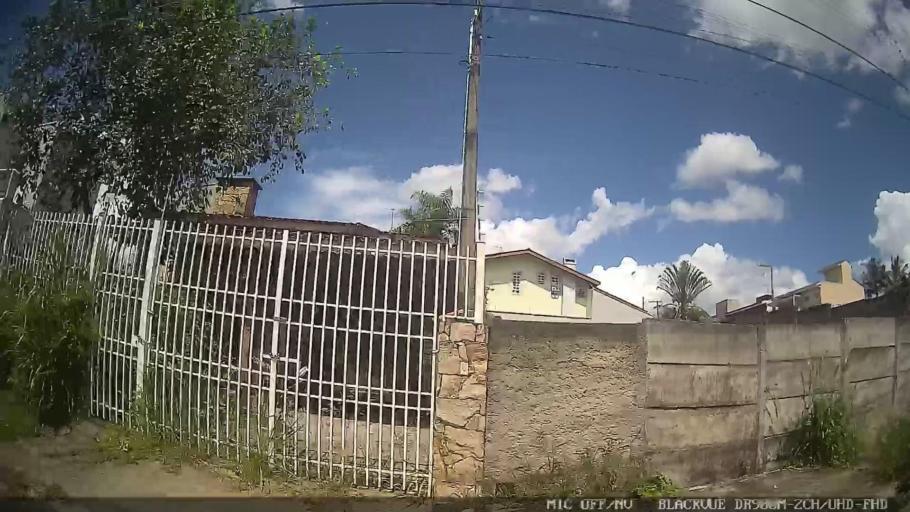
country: BR
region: Sao Paulo
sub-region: Atibaia
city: Atibaia
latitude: -23.1324
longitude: -46.5557
